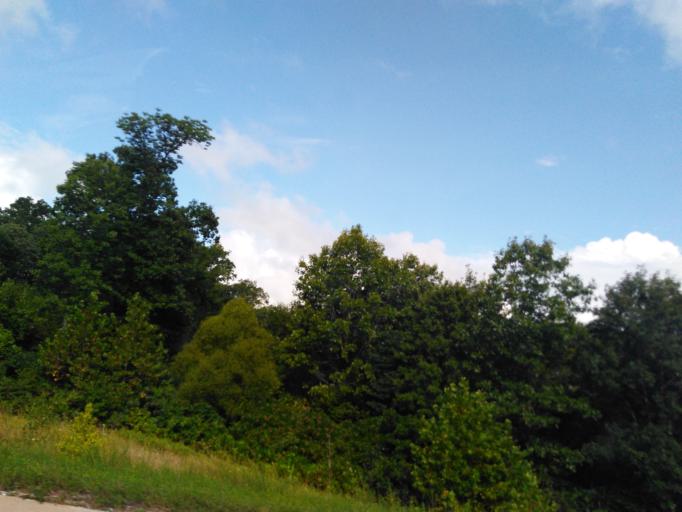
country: US
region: Missouri
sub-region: Jefferson County
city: Hillsboro
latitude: 38.2849
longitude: -90.5515
